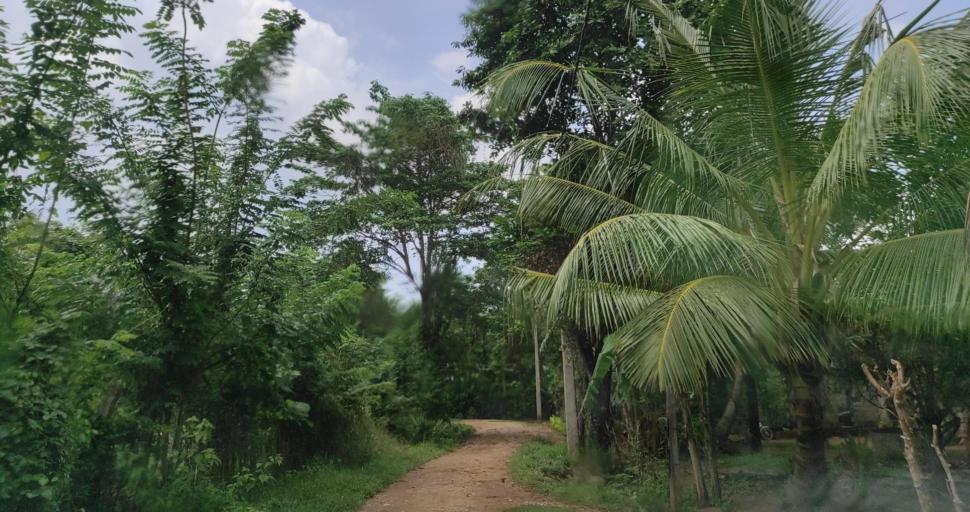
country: LK
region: Eastern Province
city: Trincomalee
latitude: 8.3716
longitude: 81.0155
